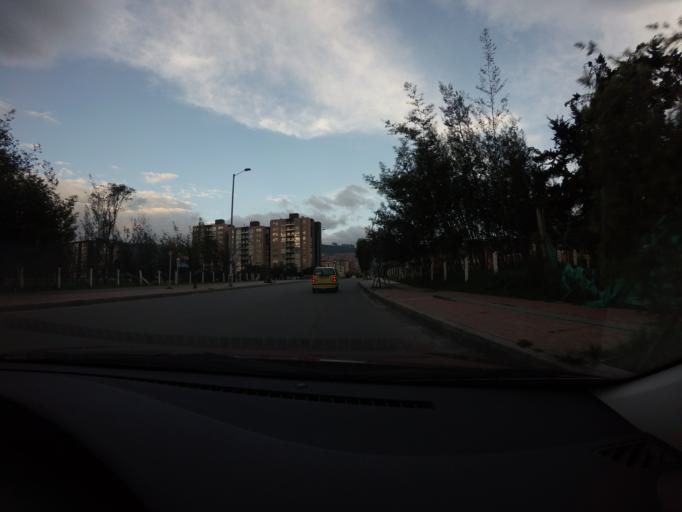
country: CO
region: Cundinamarca
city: Cota
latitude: 4.7603
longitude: -74.0416
